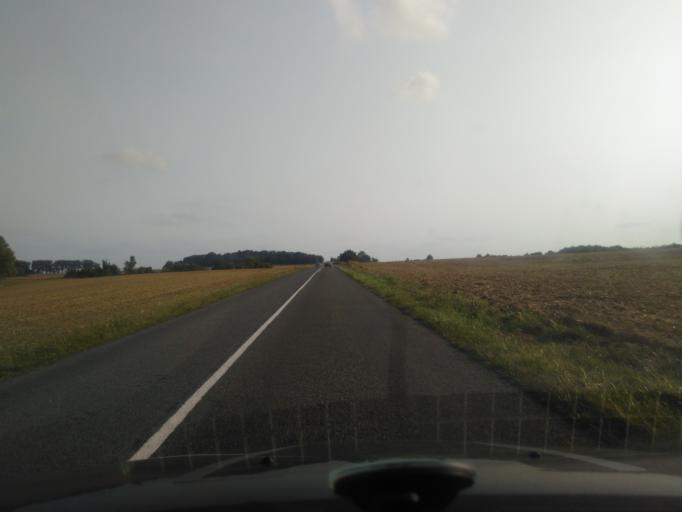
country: FR
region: Picardie
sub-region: Departement de l'Aisne
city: Bruyeres-et-Montberault
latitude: 49.5100
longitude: 3.6746
